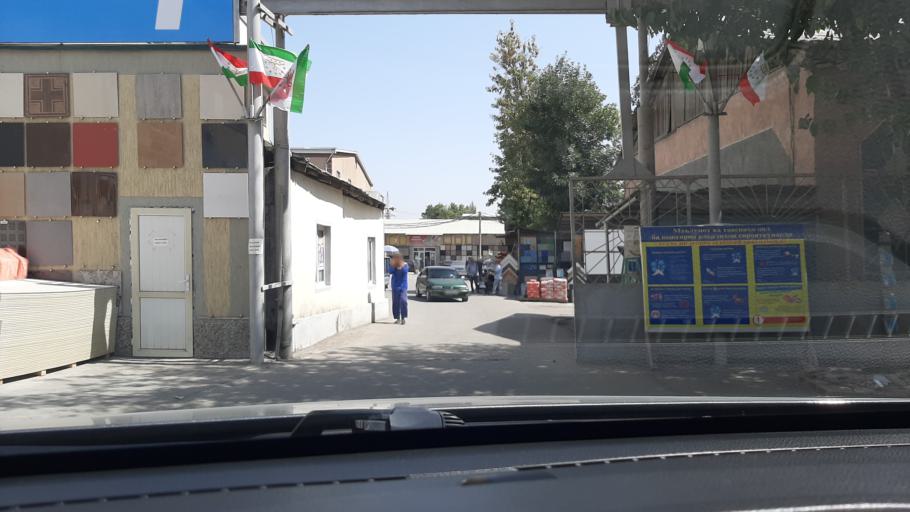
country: TJ
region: Dushanbe
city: Dushanbe
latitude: 38.5499
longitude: 68.7751
